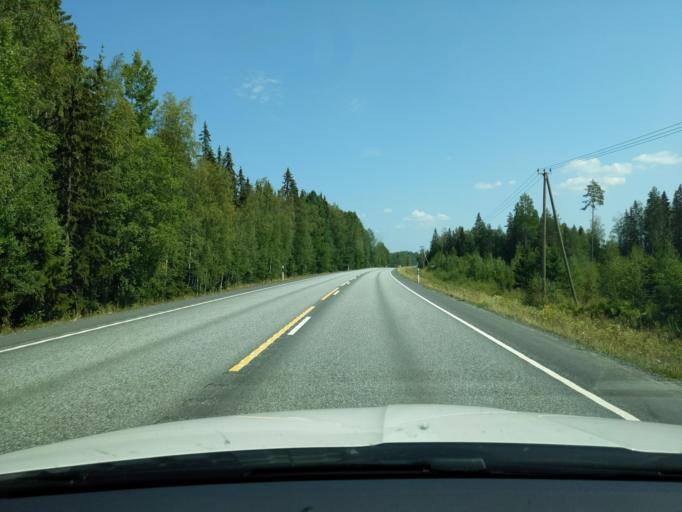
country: FI
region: Haeme
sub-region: Forssa
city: Ypaejae
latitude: 60.7700
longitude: 23.3349
